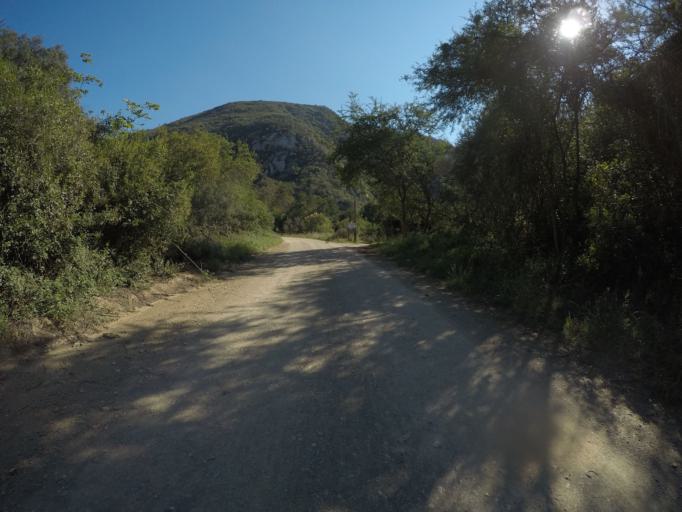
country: ZA
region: Eastern Cape
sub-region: Cacadu District Municipality
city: Kareedouw
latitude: -33.6612
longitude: 24.5407
